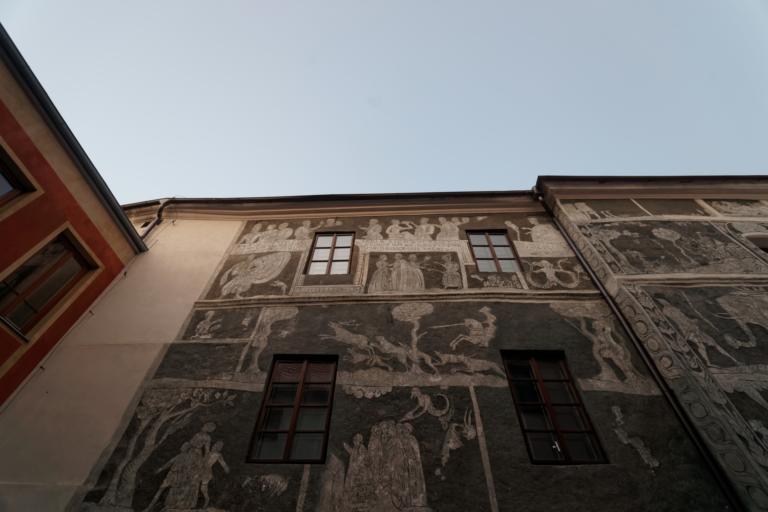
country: CZ
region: Jihocesky
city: Prachatice
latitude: 49.0132
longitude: 13.9976
